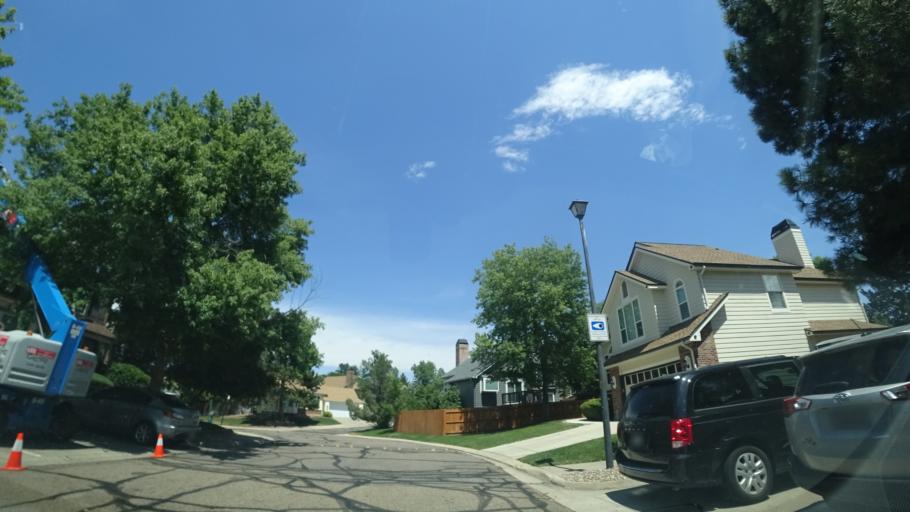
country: US
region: Colorado
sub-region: Jefferson County
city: Lakewood
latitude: 39.6942
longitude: -105.0981
